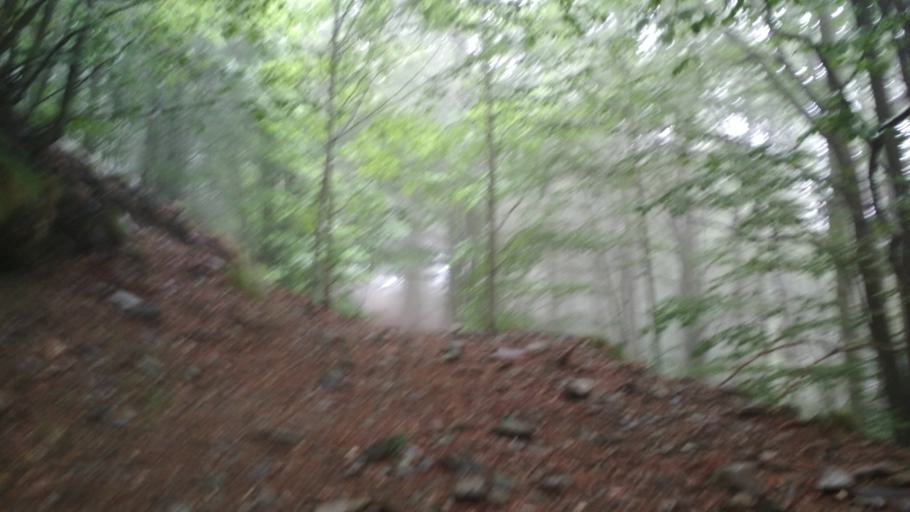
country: ES
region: Catalonia
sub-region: Provincia de Barcelona
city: Fogars de Montclus
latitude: 41.7745
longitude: 2.4407
